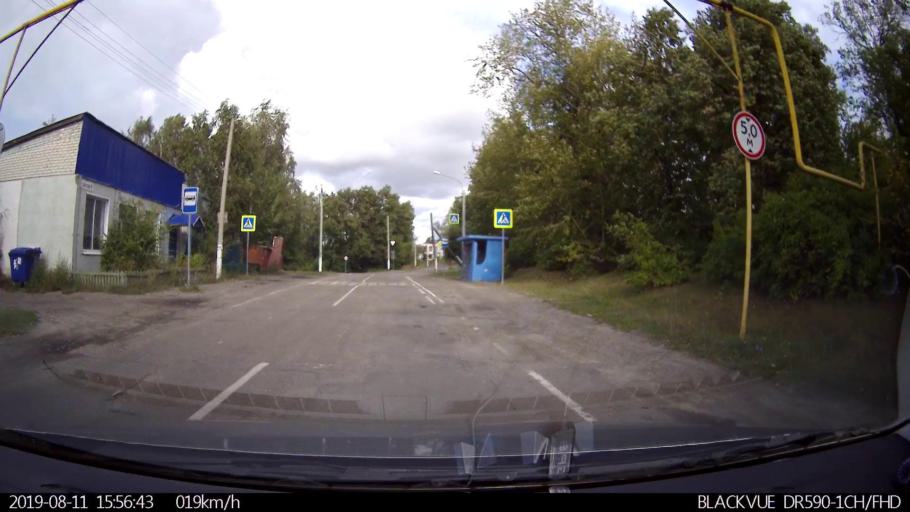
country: RU
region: Ulyanovsk
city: Ignatovka
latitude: 53.9487
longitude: 47.6514
